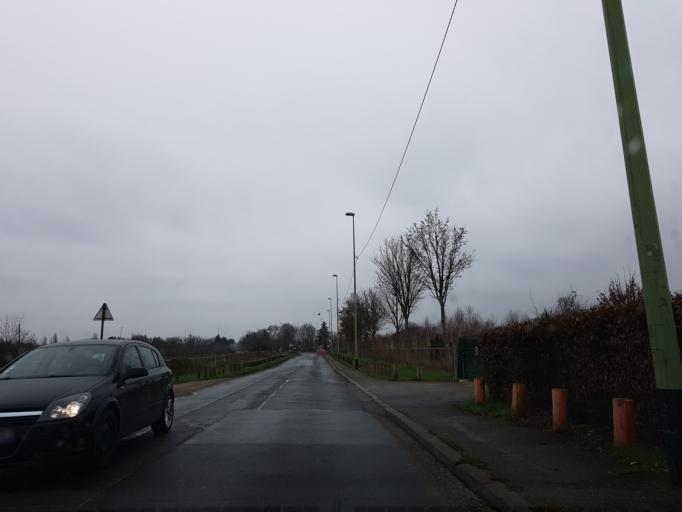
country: FR
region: Ile-de-France
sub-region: Departement du Val-de-Marne
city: Thiais
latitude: 48.7793
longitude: 2.3843
